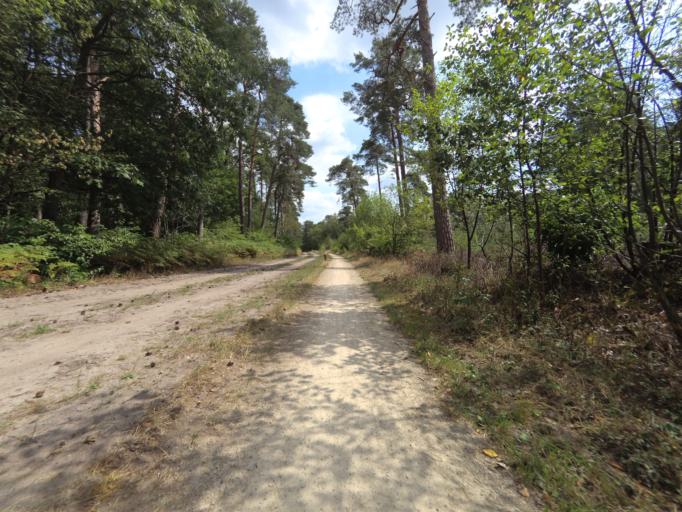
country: NL
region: Overijssel
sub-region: Gemeente Haaksbergen
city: Haaksbergen
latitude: 52.1279
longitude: 6.7138
